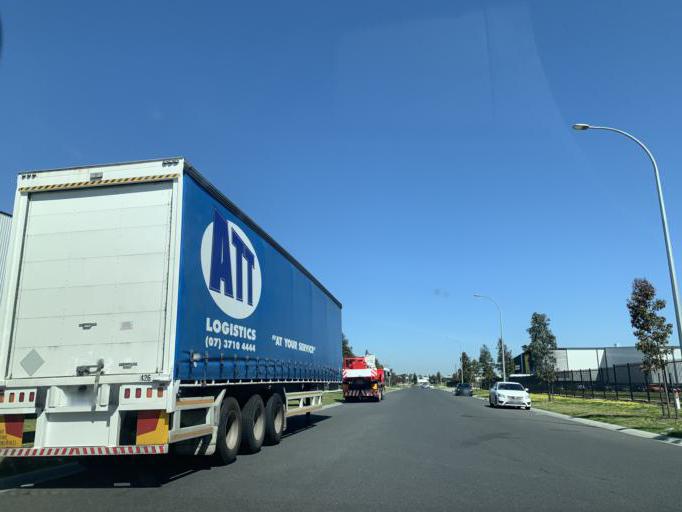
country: AU
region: Victoria
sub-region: Greater Dandenong
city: Keysborough
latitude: -38.0064
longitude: 145.1829
